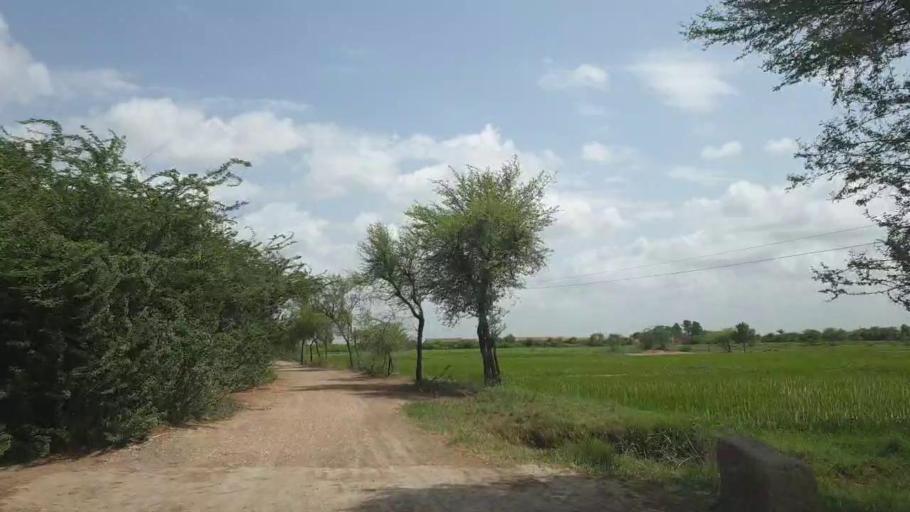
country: PK
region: Sindh
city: Tando Bago
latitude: 24.6524
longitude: 68.9928
